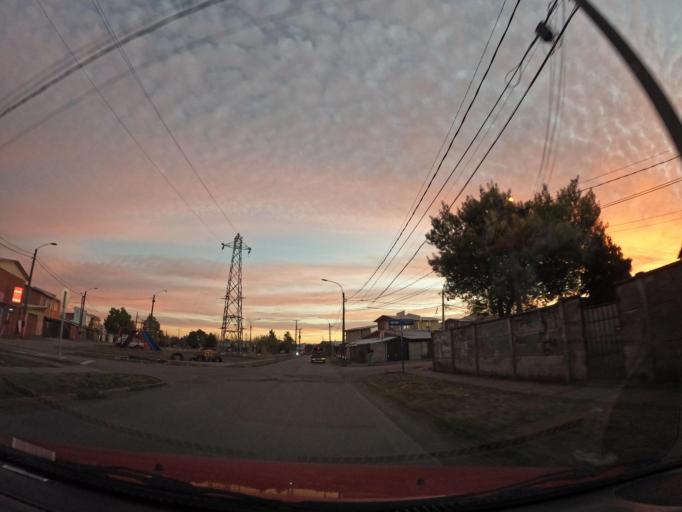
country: CL
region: Biobio
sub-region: Provincia de Nuble
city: Chillan
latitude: -36.6294
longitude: -72.0961
